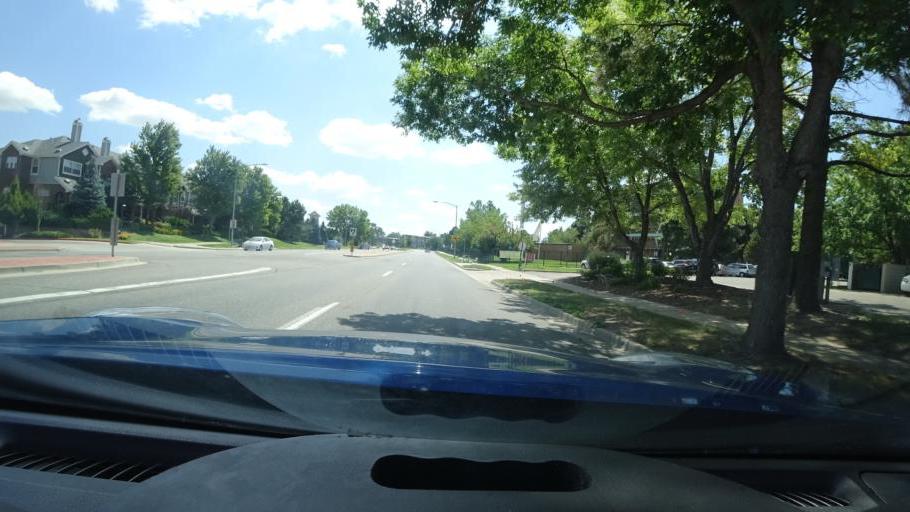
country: US
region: Colorado
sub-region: Arapahoe County
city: Glendale
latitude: 39.7084
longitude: -104.8878
